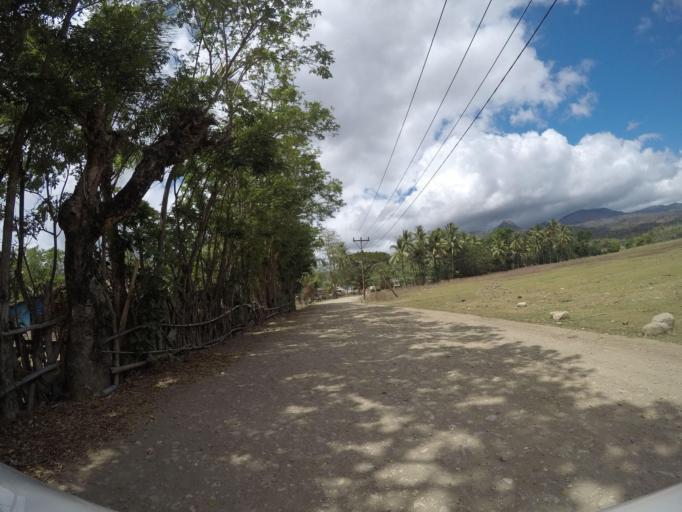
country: TL
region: Lautem
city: Lospalos
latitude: -8.5088
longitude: 126.8323
